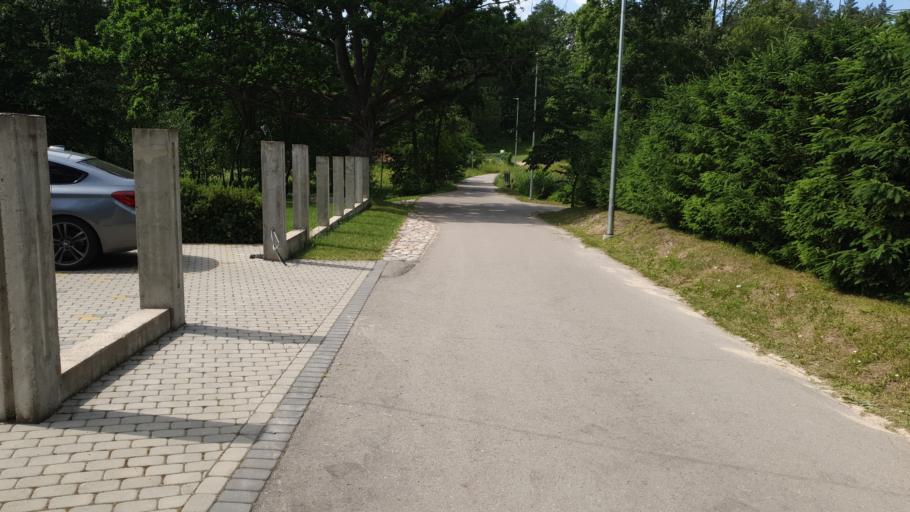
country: LT
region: Vilnius County
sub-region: Vilnius
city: Fabijoniskes
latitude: 54.7837
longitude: 25.3273
